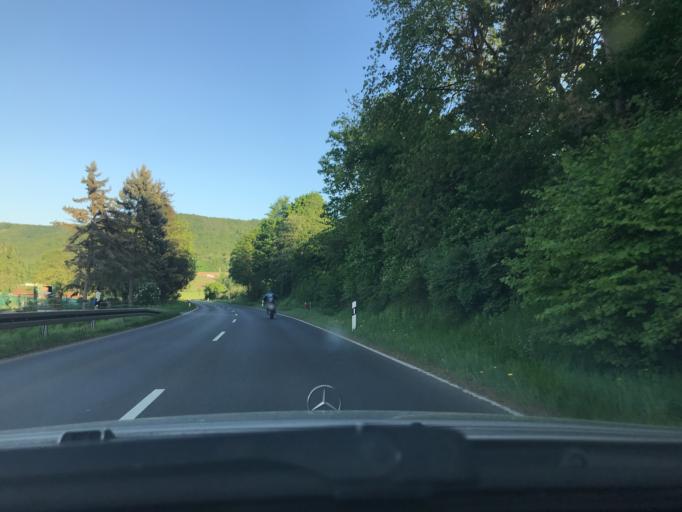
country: DE
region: Hesse
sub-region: Regierungsbezirk Kassel
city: Eschwege
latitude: 51.1767
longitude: 10.1010
